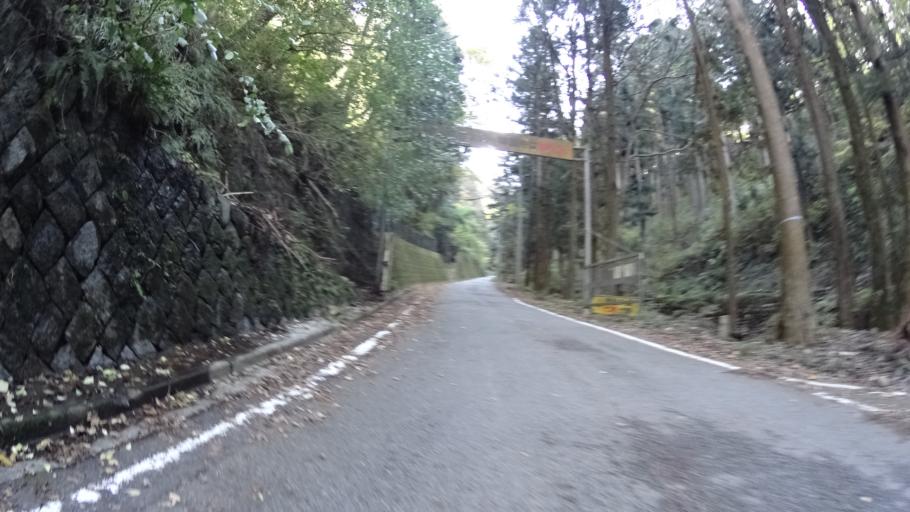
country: JP
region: Yamanashi
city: Uenohara
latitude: 35.6597
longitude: 139.1579
